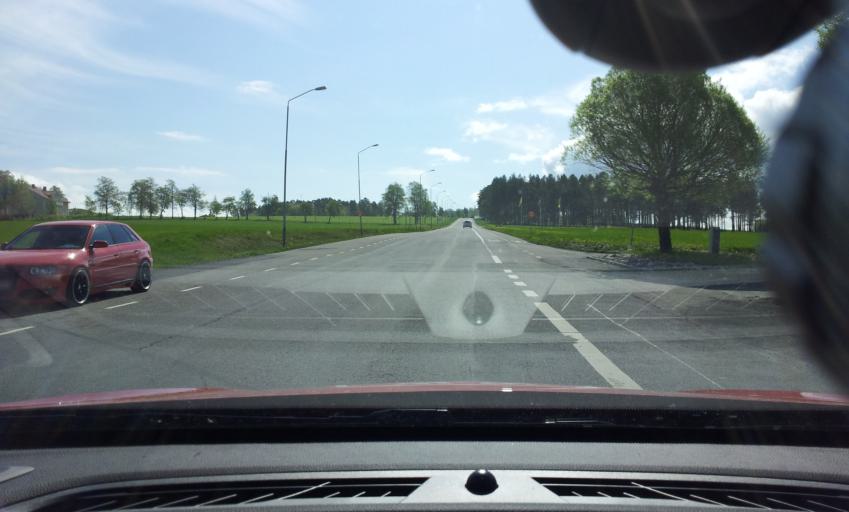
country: SE
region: Jaemtland
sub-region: OEstersunds Kommun
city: Ostersund
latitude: 63.1903
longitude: 14.4947
